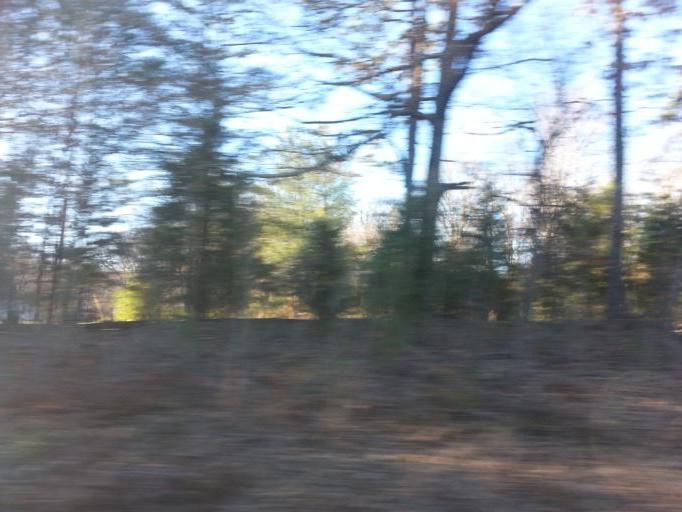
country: US
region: Tennessee
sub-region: Anderson County
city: Oak Ridge
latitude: 36.0529
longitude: -84.2414
